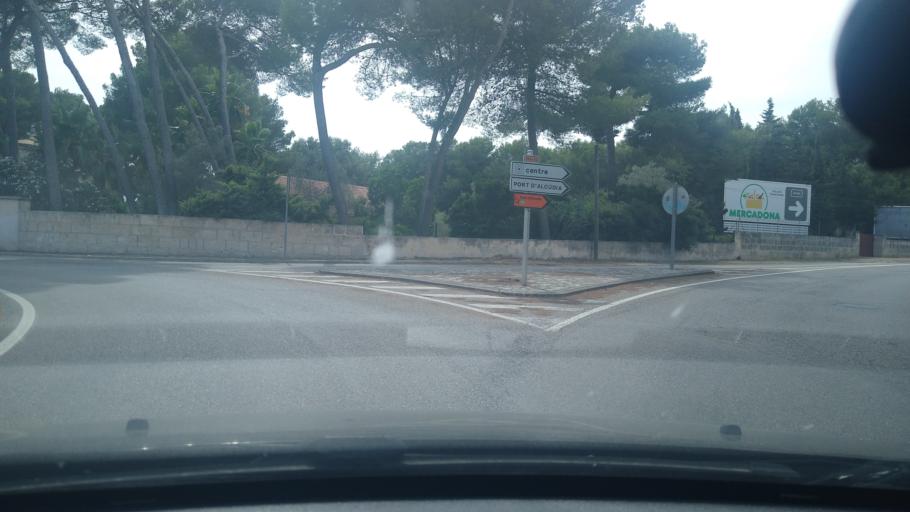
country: ES
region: Balearic Islands
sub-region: Illes Balears
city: Santa Margalida
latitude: 39.7503
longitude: 3.1491
